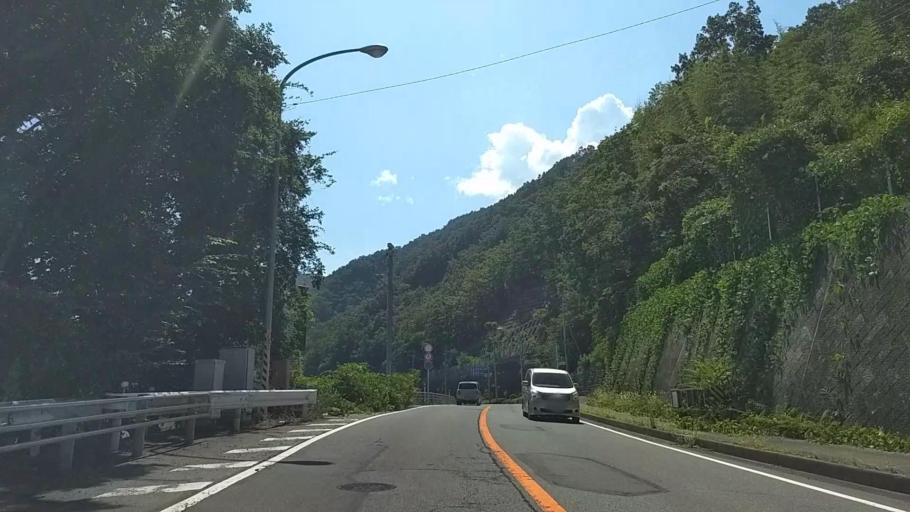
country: JP
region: Yamanashi
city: Ryuo
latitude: 35.5365
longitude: 138.4525
